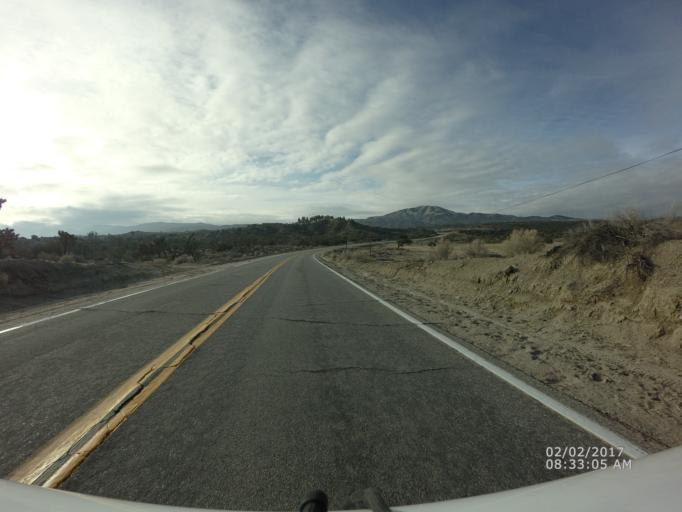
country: US
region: California
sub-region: Los Angeles County
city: Littlerock
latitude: 34.5202
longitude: -118.0277
